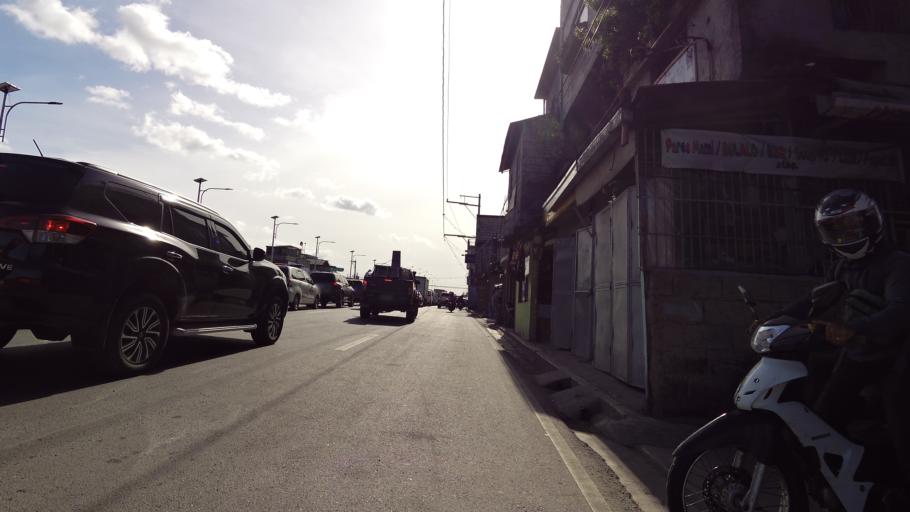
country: PH
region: Calabarzon
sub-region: Province of Rizal
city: Taytay
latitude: 14.5502
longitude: 121.1215
